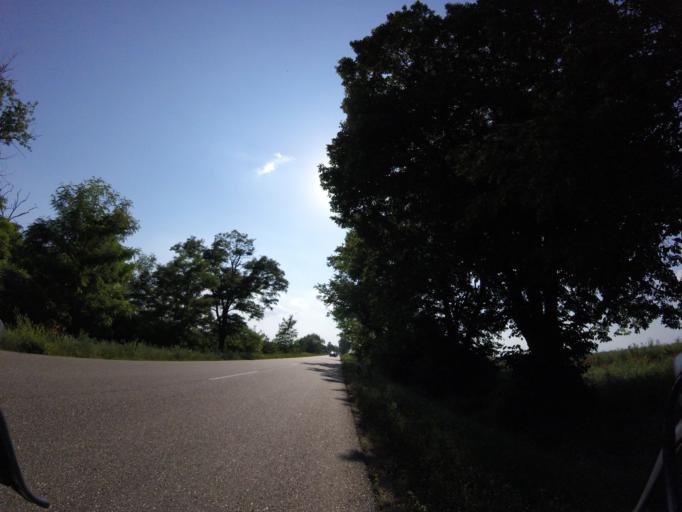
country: HU
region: Heves
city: Kiskore
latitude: 47.5587
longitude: 20.4322
